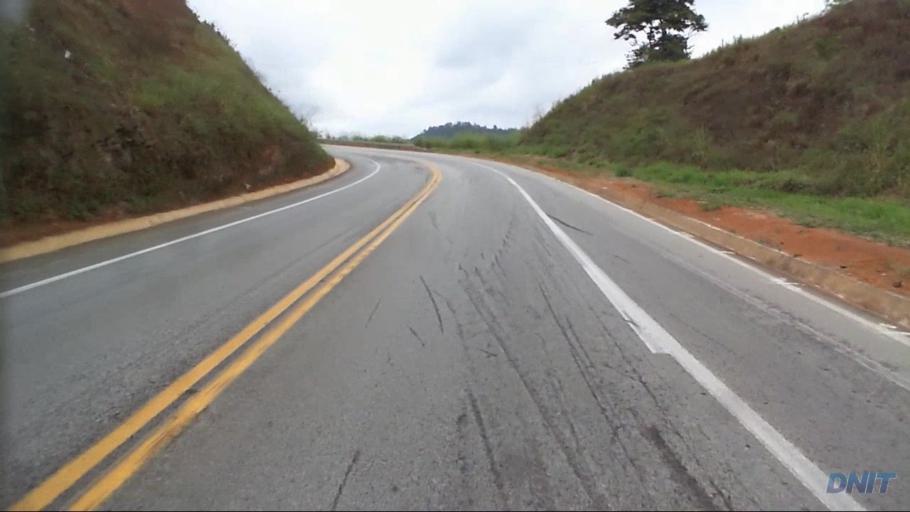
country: BR
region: Minas Gerais
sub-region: Joao Monlevade
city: Joao Monlevade
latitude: -19.8584
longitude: -43.1232
